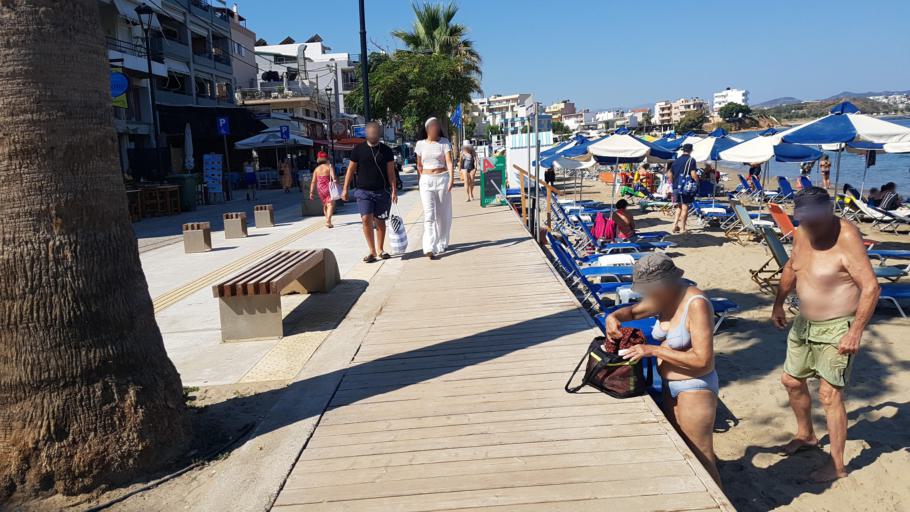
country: GR
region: Crete
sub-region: Nomos Chanias
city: Chania
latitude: 35.5147
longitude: 24.0076
